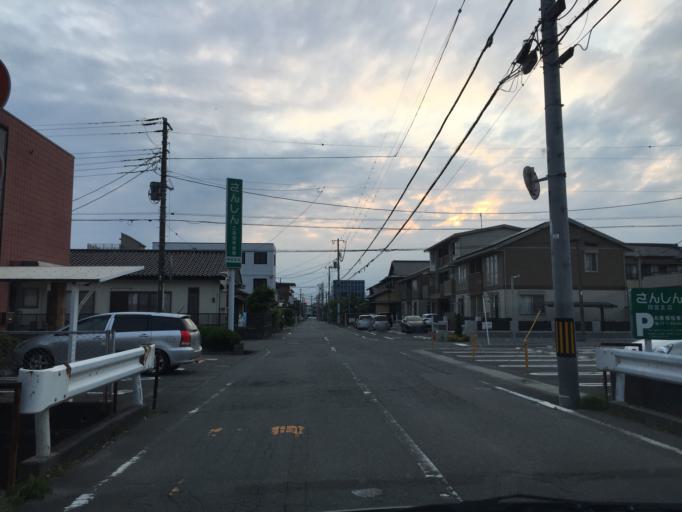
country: JP
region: Shizuoka
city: Numazu
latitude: 35.1220
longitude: 138.8719
